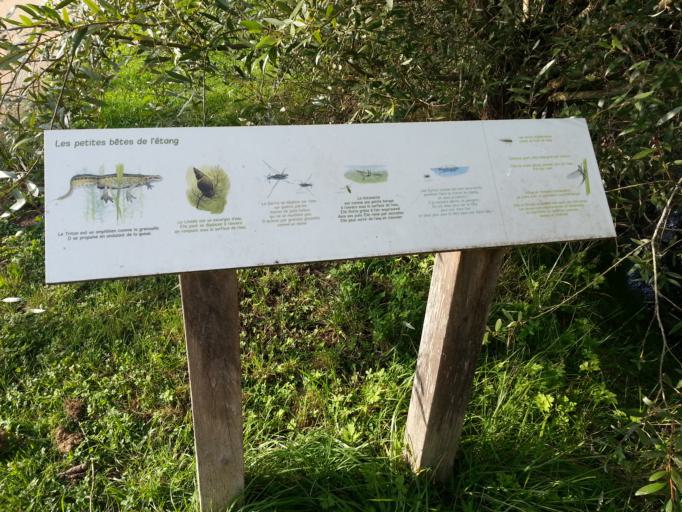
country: FR
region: Bourgogne
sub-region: Departement de Saone-et-Loire
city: Chatenoy-le-Royal
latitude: 46.7747
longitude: 4.7975
